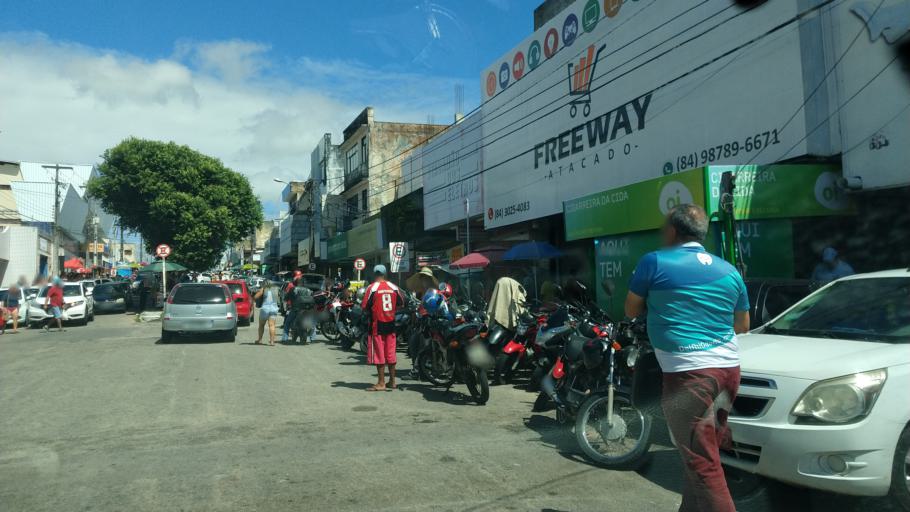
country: BR
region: Rio Grande do Norte
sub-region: Natal
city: Natal
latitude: -5.7961
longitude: -35.2185
